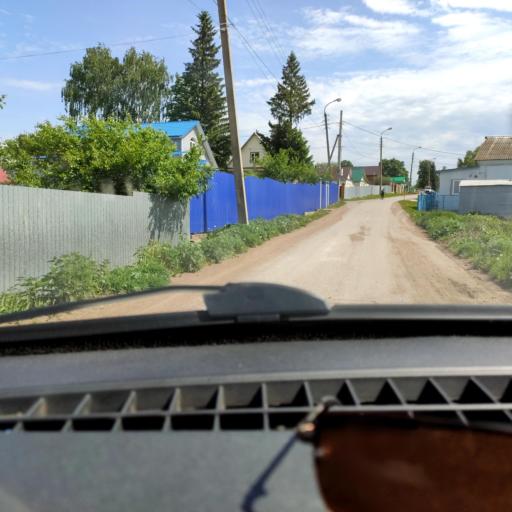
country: RU
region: Bashkortostan
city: Iglino
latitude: 54.7868
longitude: 56.2267
